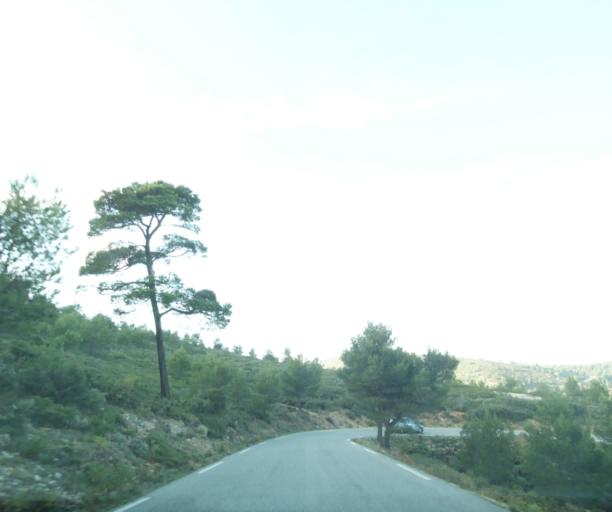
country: FR
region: Provence-Alpes-Cote d'Azur
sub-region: Departement des Bouches-du-Rhone
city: Cassis
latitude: 43.2043
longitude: 5.5650
